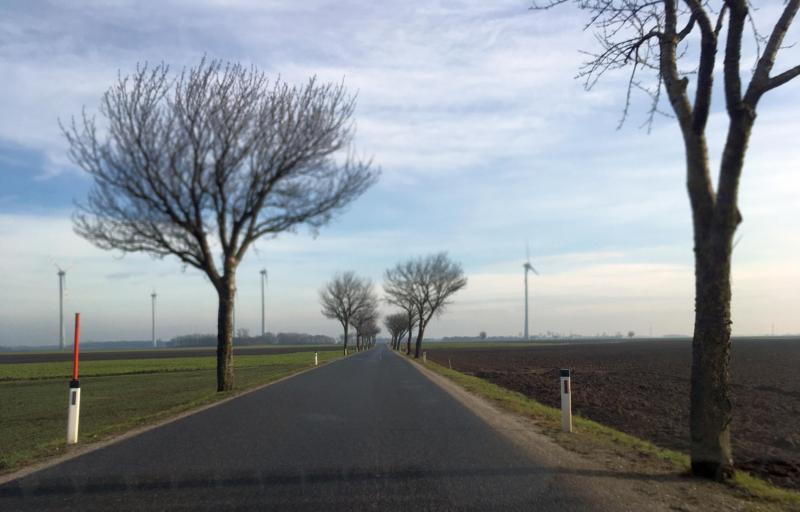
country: AT
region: Lower Austria
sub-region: Politischer Bezirk Ganserndorf
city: Andlersdorf
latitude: 48.1928
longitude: 16.6627
